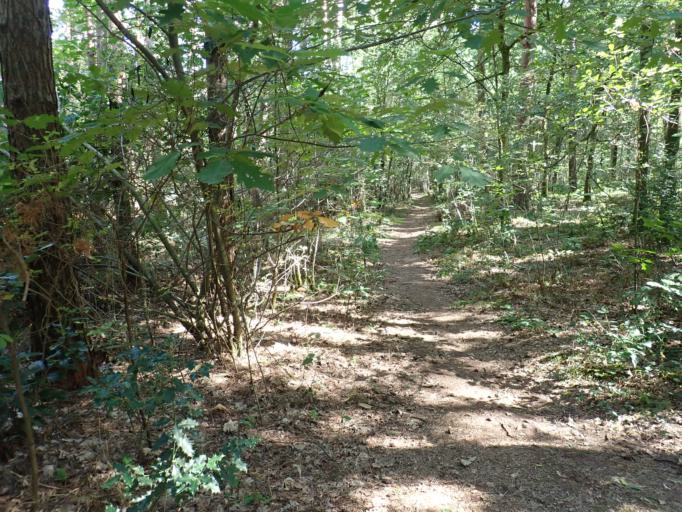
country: BE
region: Flanders
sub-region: Provincie Antwerpen
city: Kasterlee
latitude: 51.2175
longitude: 4.9037
